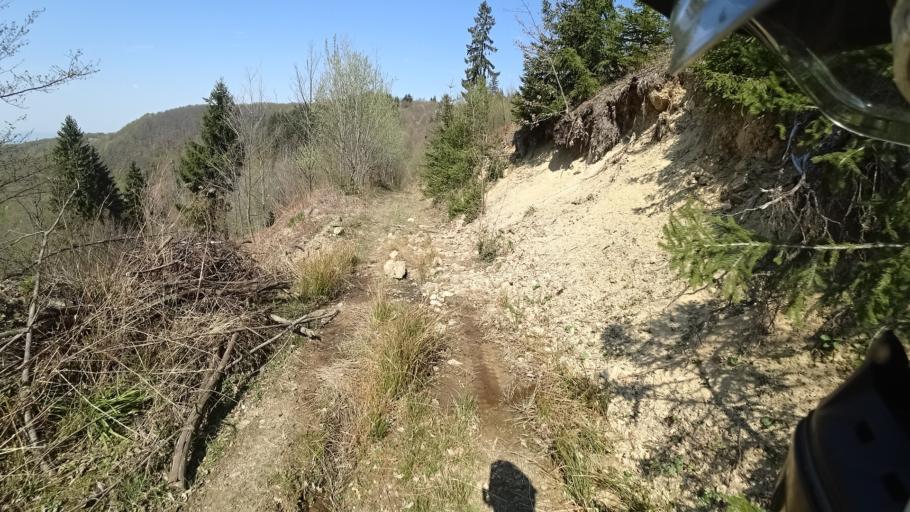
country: HR
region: Zagrebacka
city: Jablanovec
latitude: 45.8902
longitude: 15.9184
